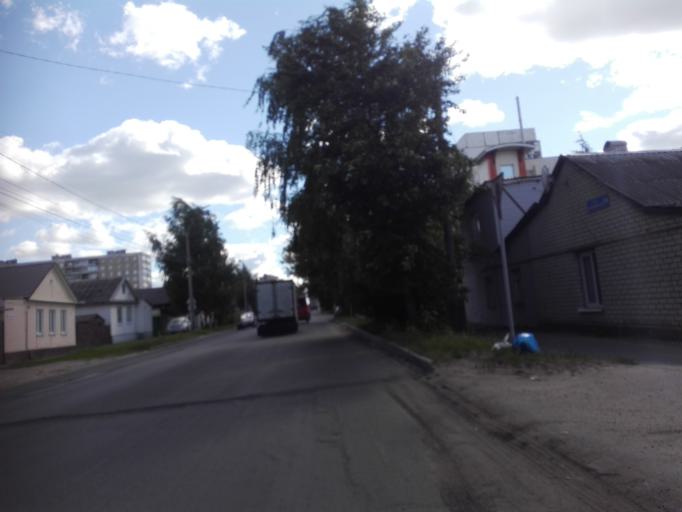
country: RU
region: Orjol
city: Orel
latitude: 52.9529
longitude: 36.0455
